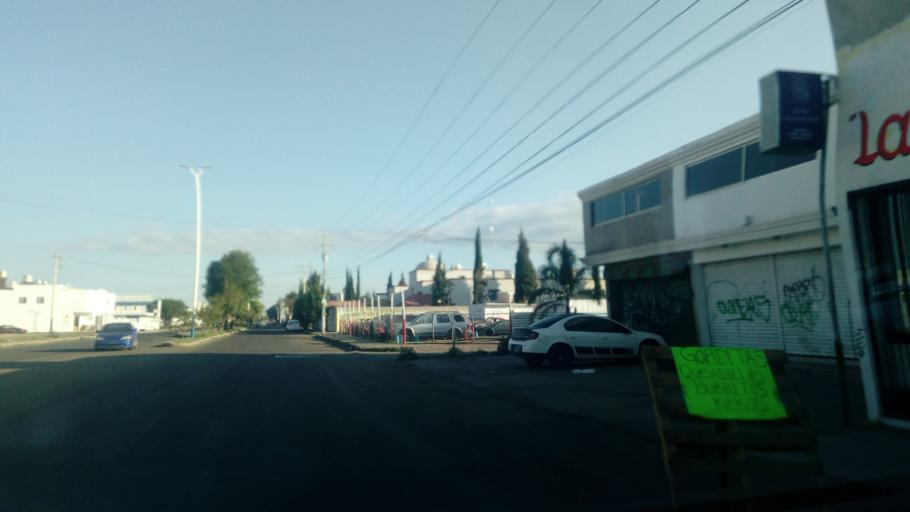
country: MX
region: Durango
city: Victoria de Durango
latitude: 24.0391
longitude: -104.6086
